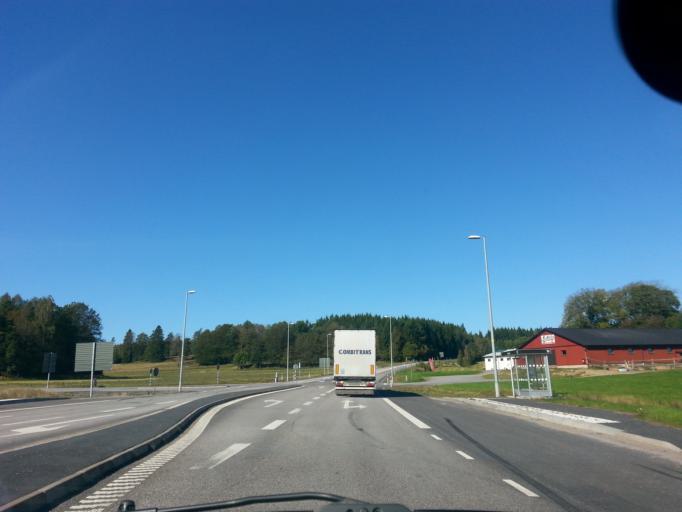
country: SE
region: Vaestra Goetaland
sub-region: Harryda Kommun
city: Ravlanda
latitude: 57.5544
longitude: 12.5226
